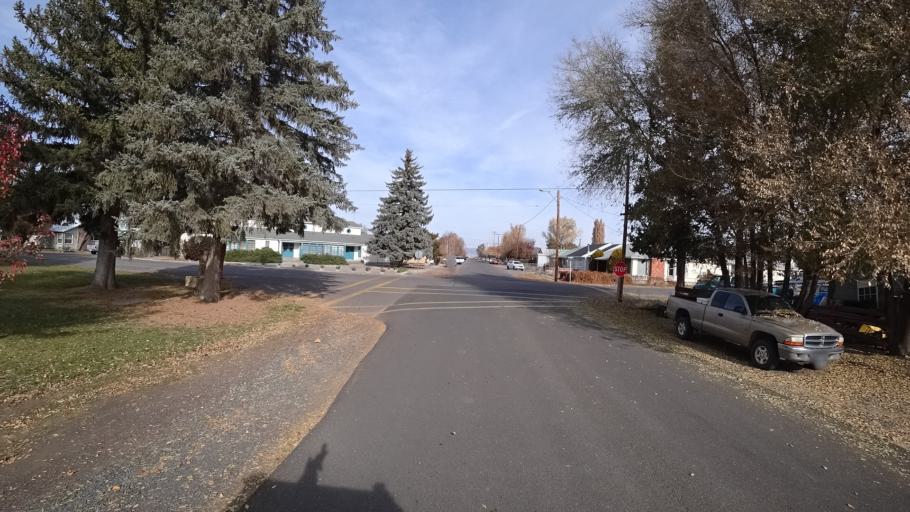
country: US
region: California
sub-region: Siskiyou County
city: Tulelake
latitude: 41.9570
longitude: -121.4792
